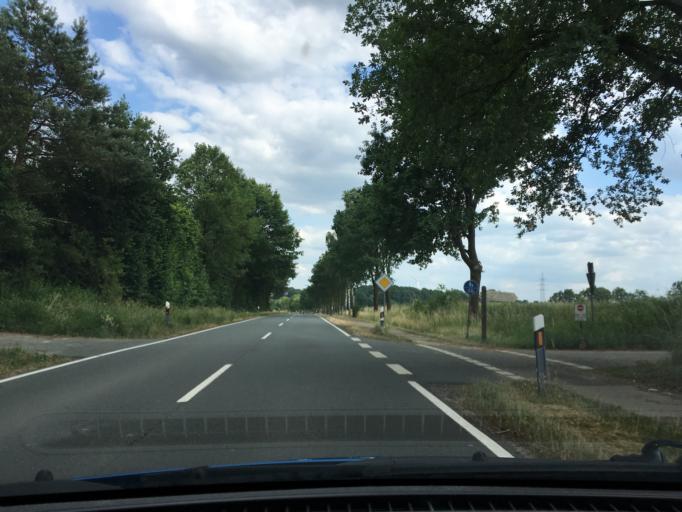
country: DE
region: Lower Saxony
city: Soderstorf
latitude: 53.1340
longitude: 10.1588
